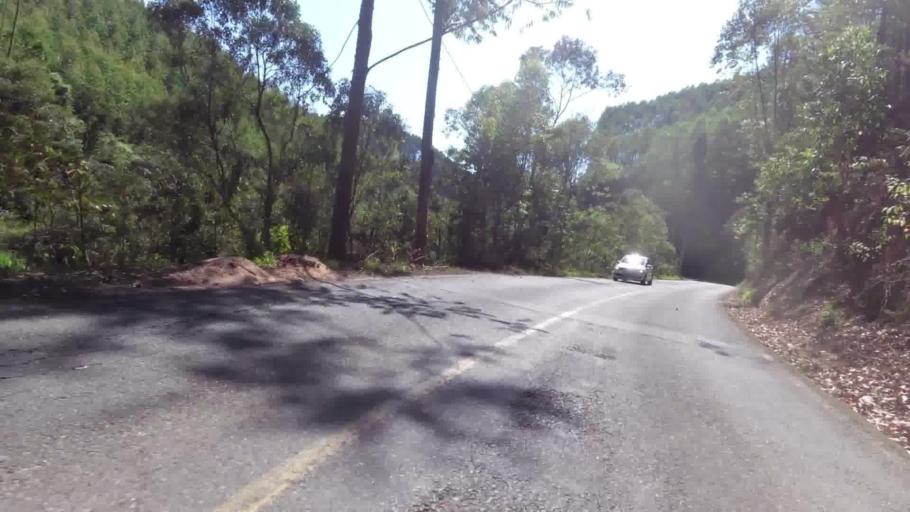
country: BR
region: Espirito Santo
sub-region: Marechal Floriano
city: Marechal Floriano
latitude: -20.4385
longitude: -40.8815
